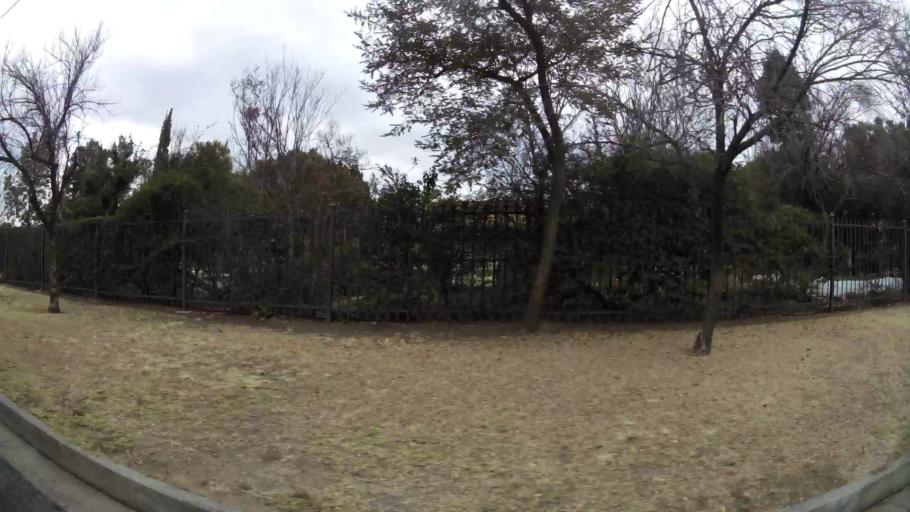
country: ZA
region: Orange Free State
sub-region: Fezile Dabi District Municipality
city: Kroonstad
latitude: -27.6787
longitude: 27.2478
